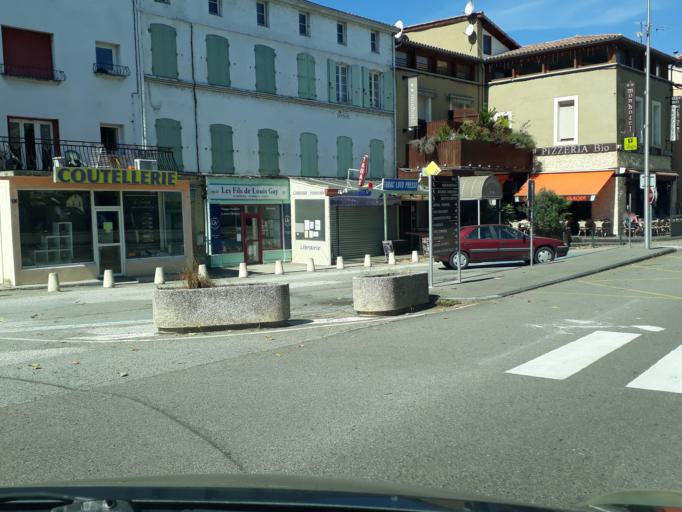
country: FR
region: Rhone-Alpes
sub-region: Departement de l'Ardeche
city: Serrieres
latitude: 45.3183
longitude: 4.7655
